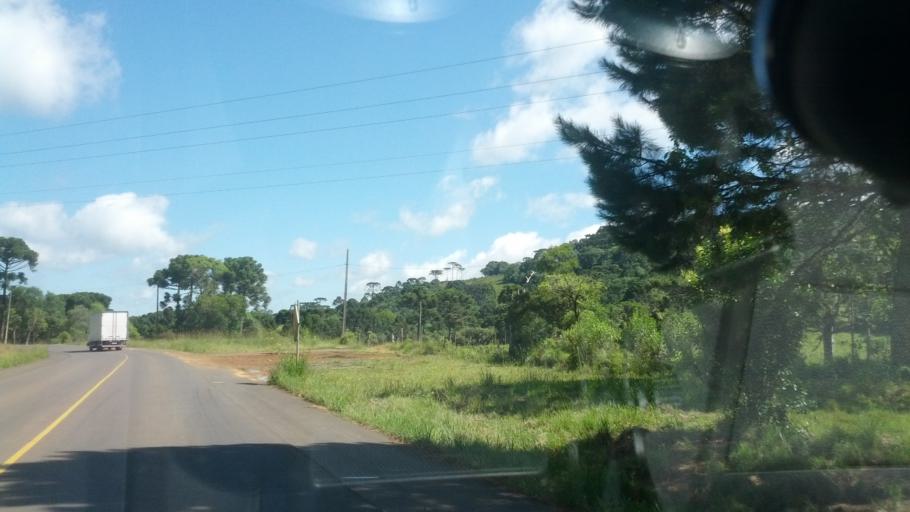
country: BR
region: Santa Catarina
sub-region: Lages
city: Lages
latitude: -27.9323
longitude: -50.5289
